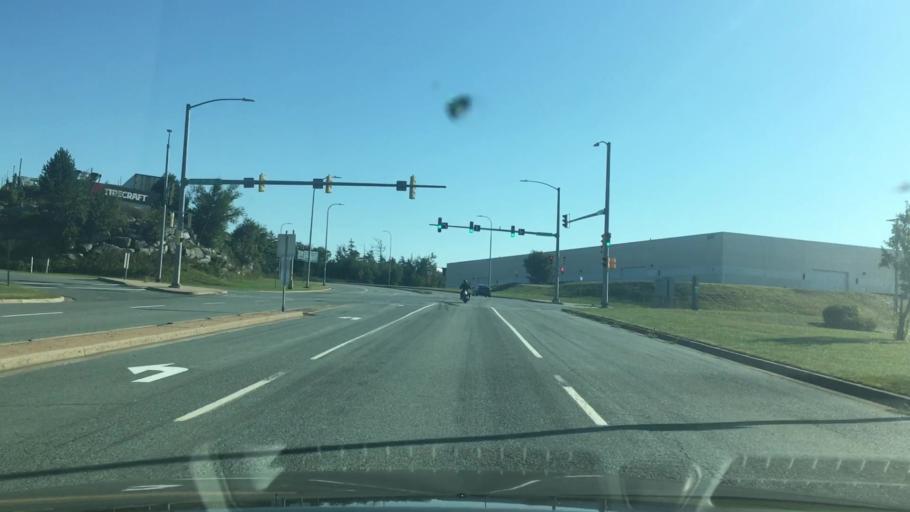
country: CA
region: Nova Scotia
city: Dartmouth
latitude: 44.7173
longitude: -63.5829
